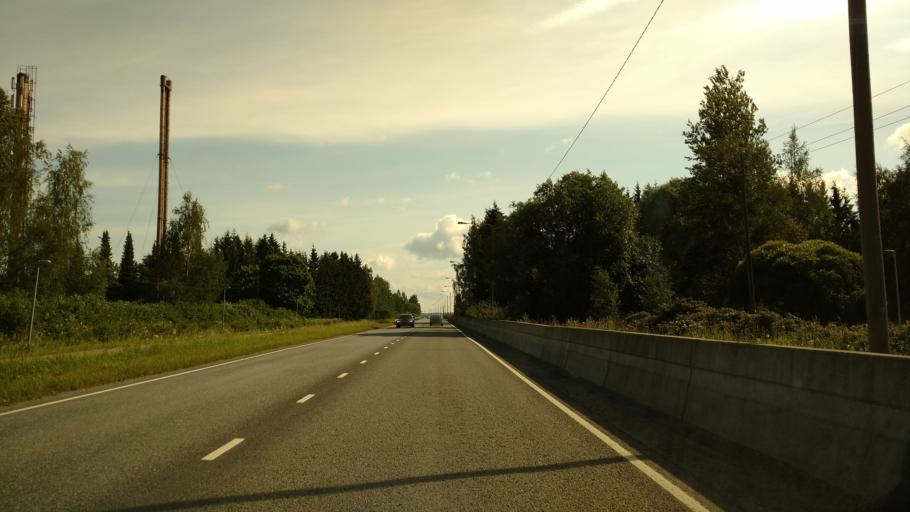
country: FI
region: Varsinais-Suomi
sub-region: Salo
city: Salo
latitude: 60.3988
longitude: 23.1404
